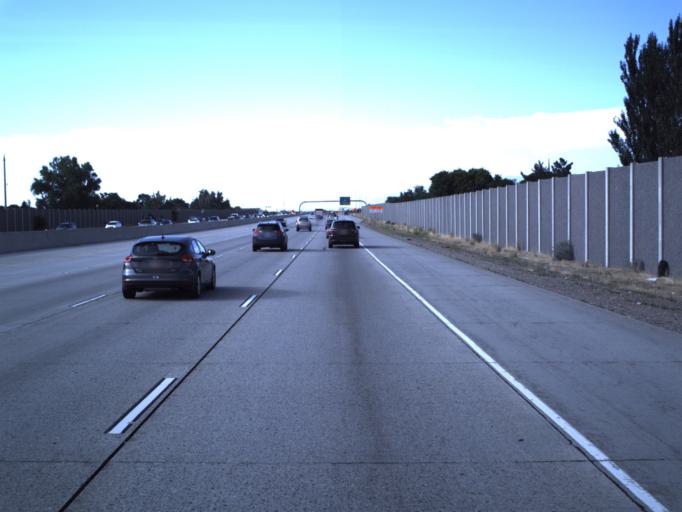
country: US
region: Utah
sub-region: Salt Lake County
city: Taylorsville
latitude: 40.6584
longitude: -111.9524
